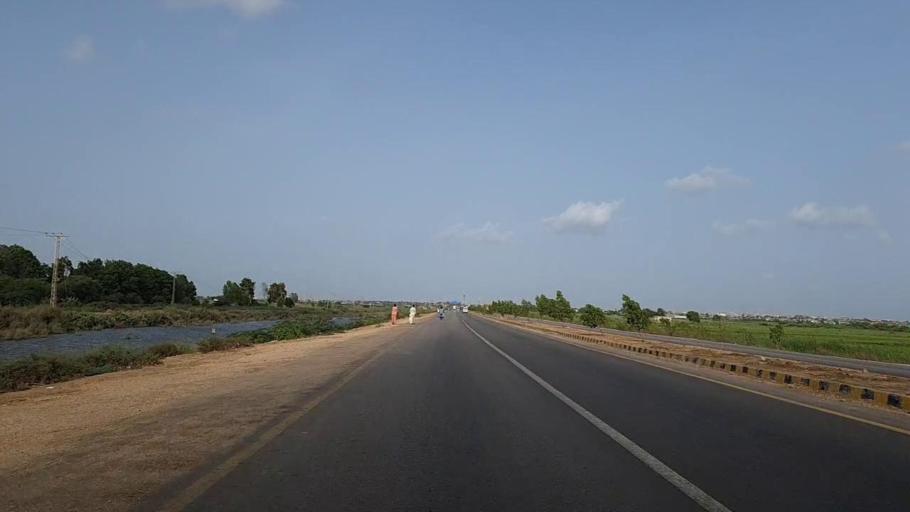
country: PK
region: Sindh
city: Thatta
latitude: 24.7454
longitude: 67.8625
